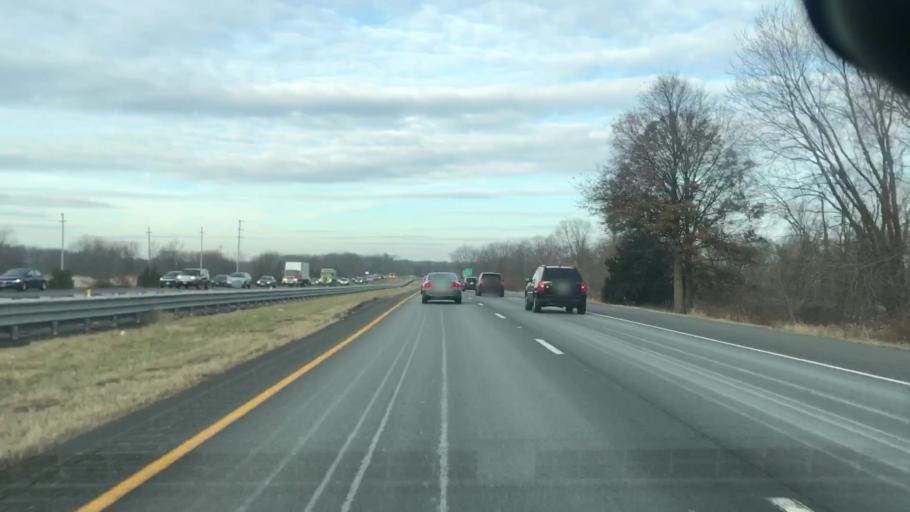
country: US
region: New Jersey
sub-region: Morris County
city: East Hanover
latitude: 40.8431
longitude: -74.3433
